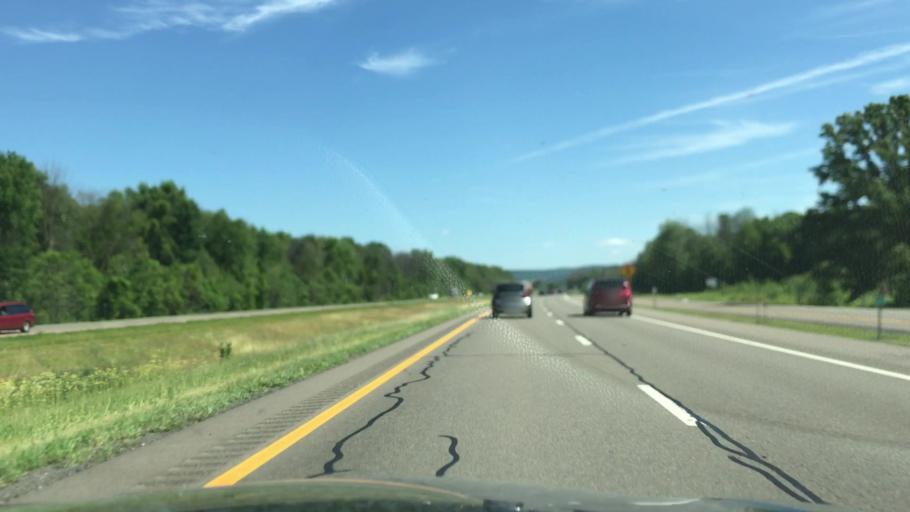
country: US
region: New York
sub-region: Steuben County
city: Gang Mills
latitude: 42.2430
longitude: -77.1976
